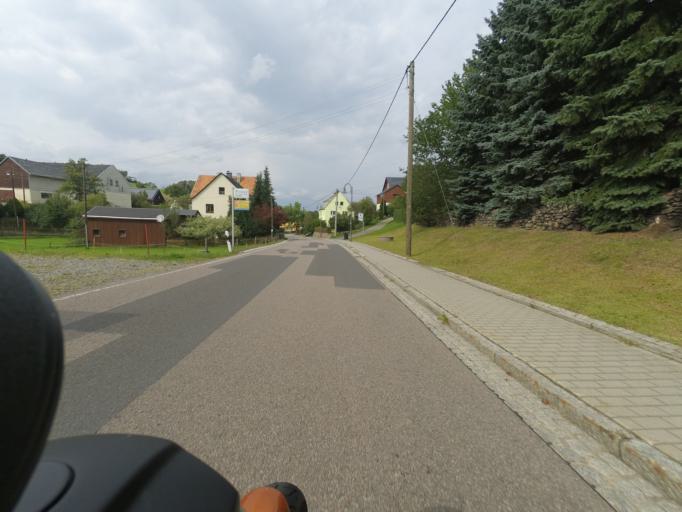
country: DE
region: Saxony
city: Barenstein
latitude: 50.8281
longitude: 13.8056
